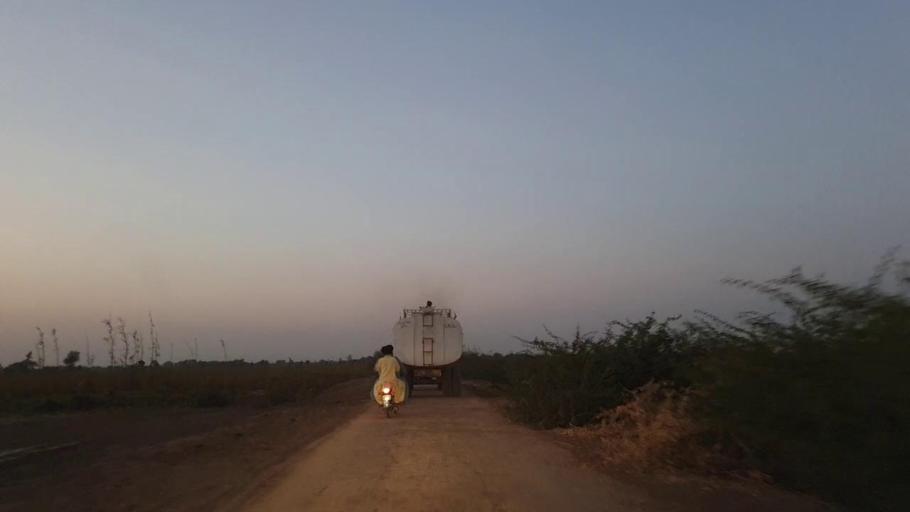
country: PK
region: Sindh
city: Naukot
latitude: 24.9009
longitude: 69.3802
